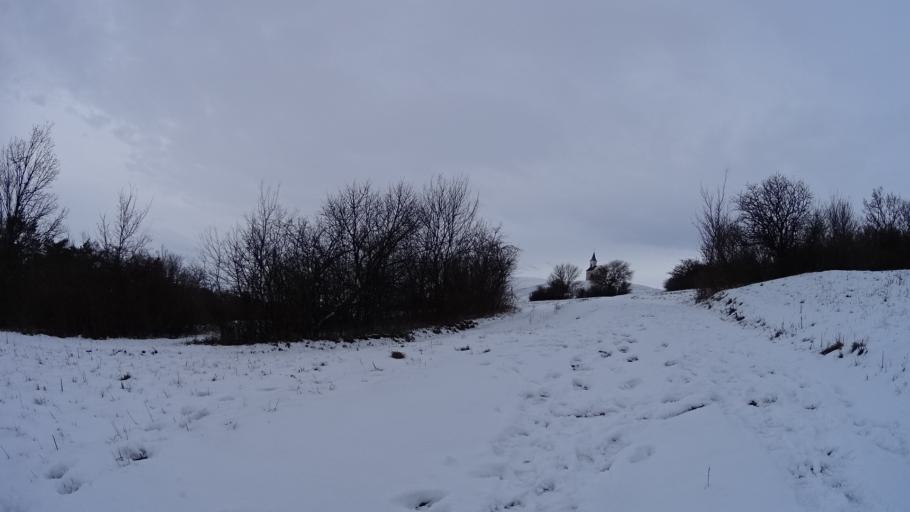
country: AT
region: Lower Austria
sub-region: Politischer Bezirk Korneuburg
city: Niederhollabrunn
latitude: 48.4279
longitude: 16.2895
